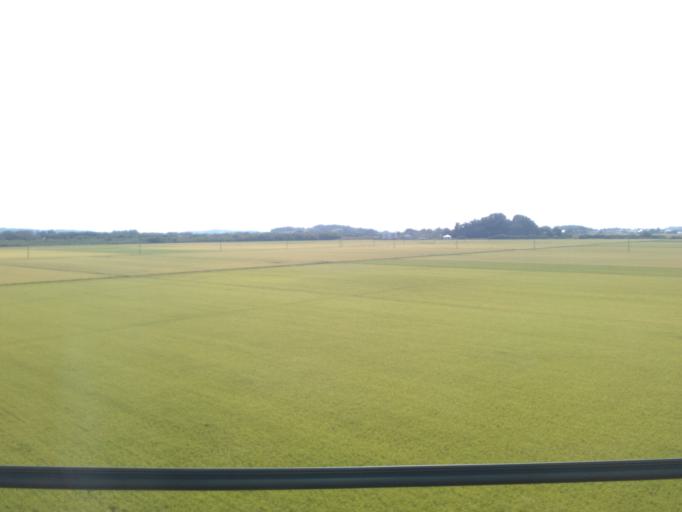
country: JP
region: Iwate
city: Ichinoseki
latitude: 38.7819
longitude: 141.0903
